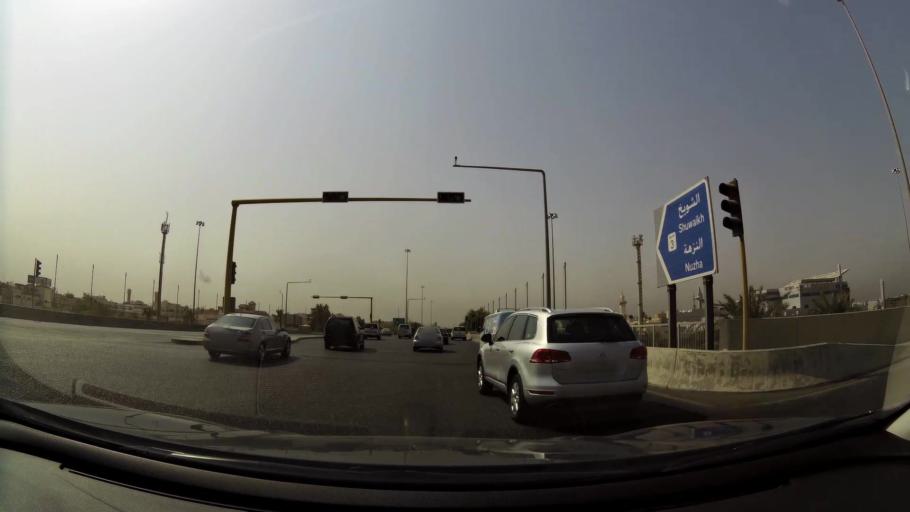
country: KW
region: Al Asimah
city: Ad Dasmah
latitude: 29.3407
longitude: 48.0009
